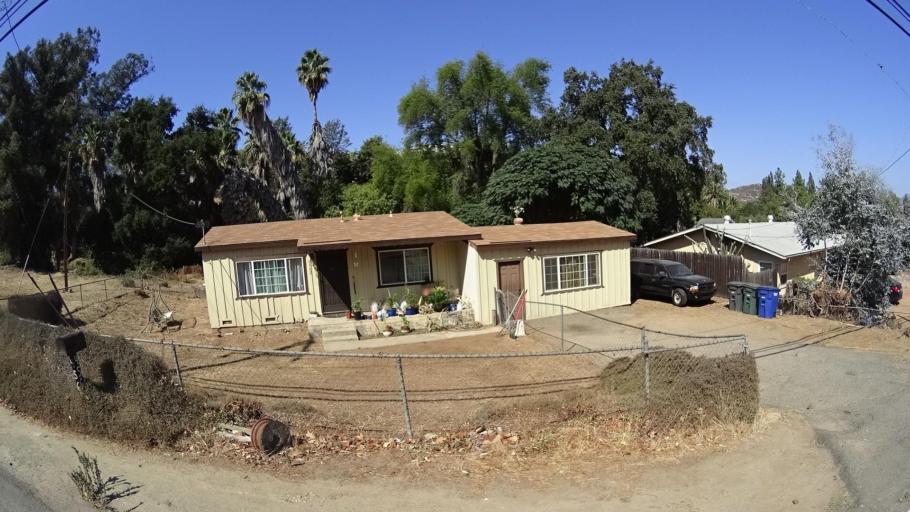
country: US
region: California
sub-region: San Diego County
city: Lakeside
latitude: 32.8501
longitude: -116.9409
